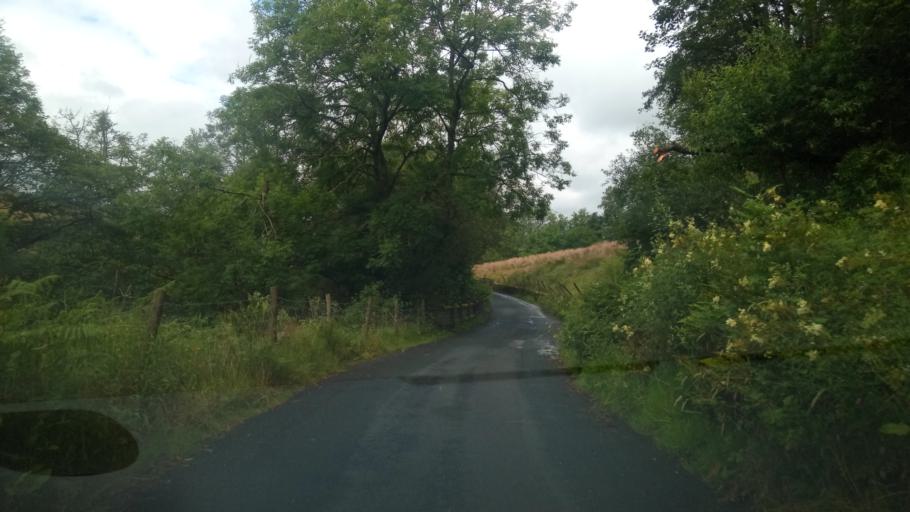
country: GB
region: England
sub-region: North Yorkshire
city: Ingleton
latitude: 54.2554
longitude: -2.3430
